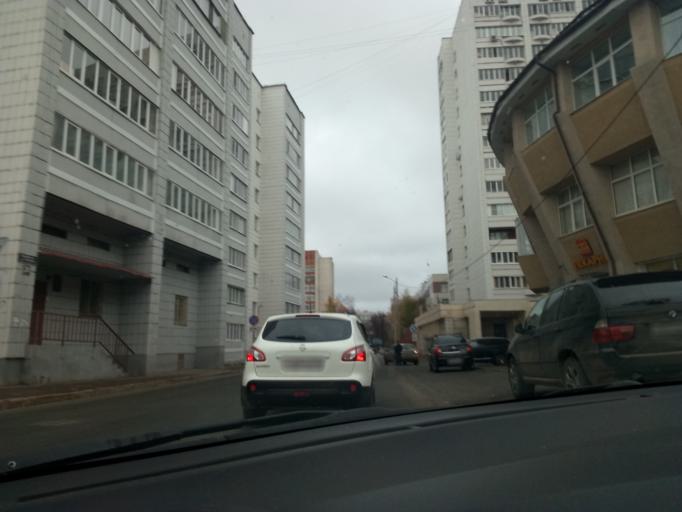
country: RU
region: Tatarstan
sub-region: Gorod Kazan'
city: Kazan
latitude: 55.7867
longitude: 49.1509
